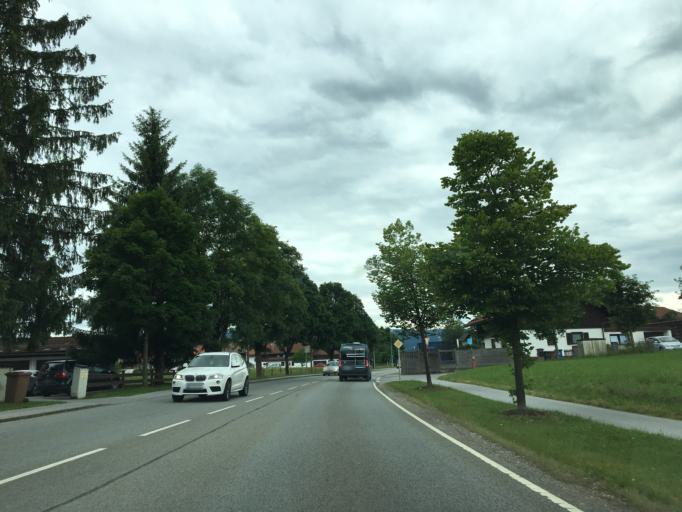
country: DE
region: Bavaria
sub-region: Upper Bavaria
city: Miesbach
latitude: 47.7856
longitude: 11.8365
